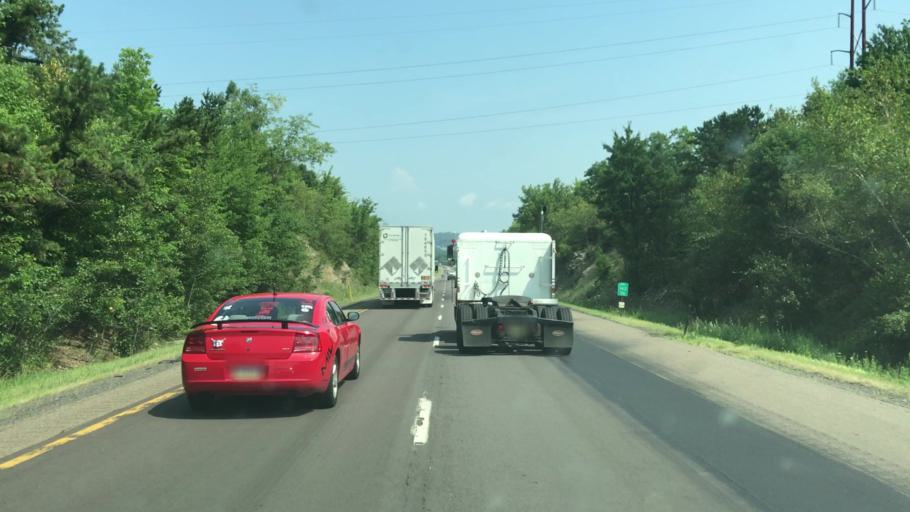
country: US
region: Pennsylvania
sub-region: Luzerne County
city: West Hazleton
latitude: 40.9520
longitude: -76.0265
